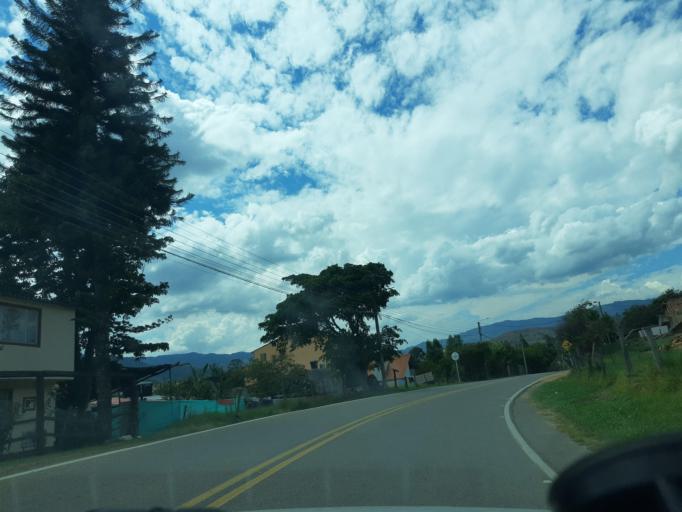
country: CO
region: Boyaca
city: Raquira
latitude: 5.5723
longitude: -73.6515
